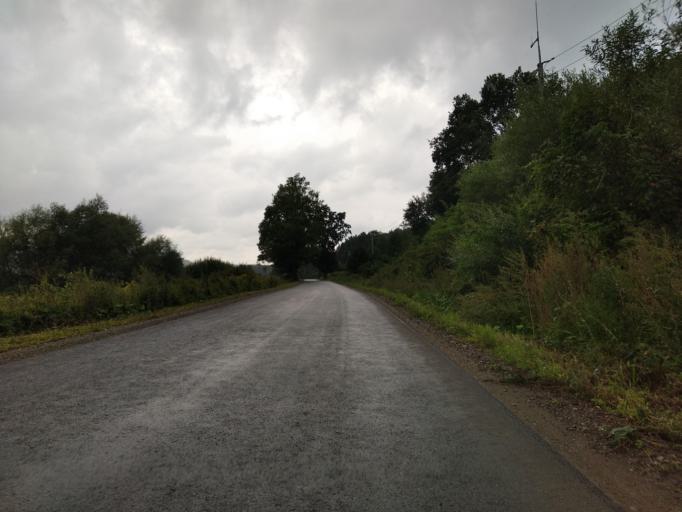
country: PL
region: Subcarpathian Voivodeship
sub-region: Powiat brzozowski
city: Dydnia
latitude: 49.6786
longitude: 22.2688
